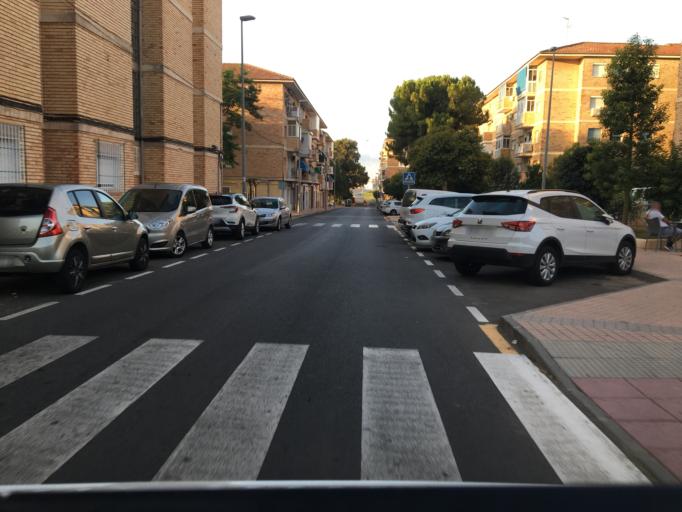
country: ES
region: Murcia
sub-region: Murcia
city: Cartagena
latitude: 37.6251
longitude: -0.9834
